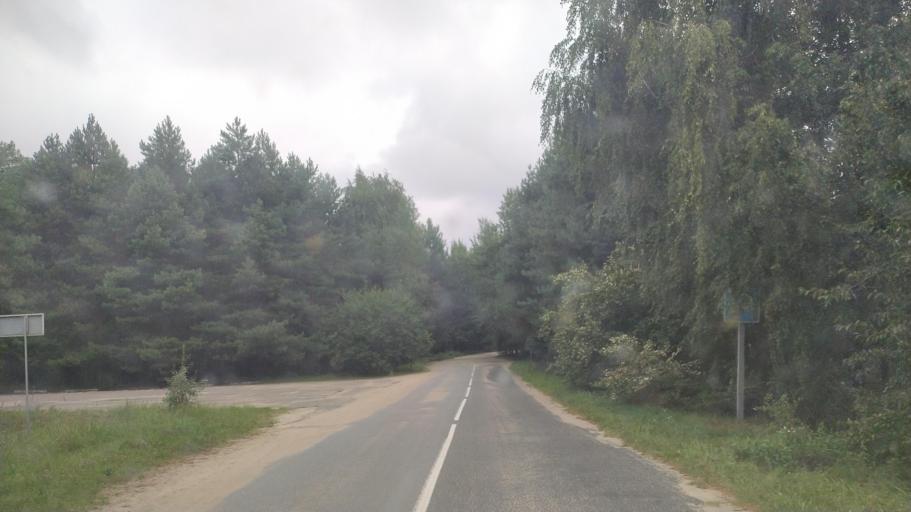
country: BY
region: Brest
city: Byaroza
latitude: 52.6006
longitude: 24.8776
